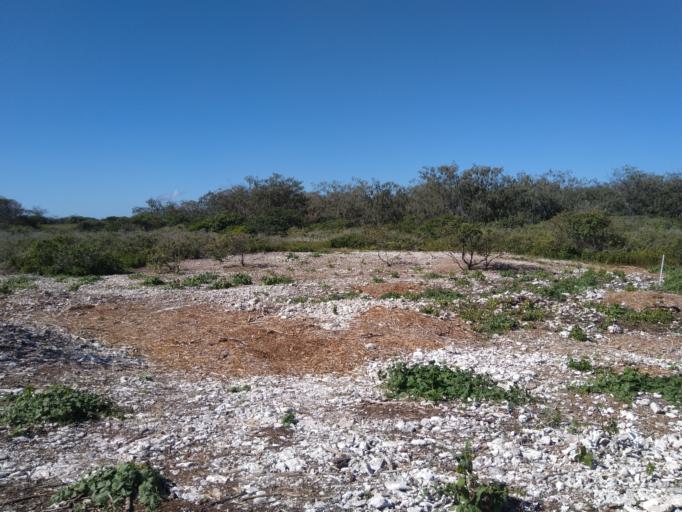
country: AU
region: Queensland
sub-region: Bundaberg
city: Bundaberg
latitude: -24.1110
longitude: 152.7134
